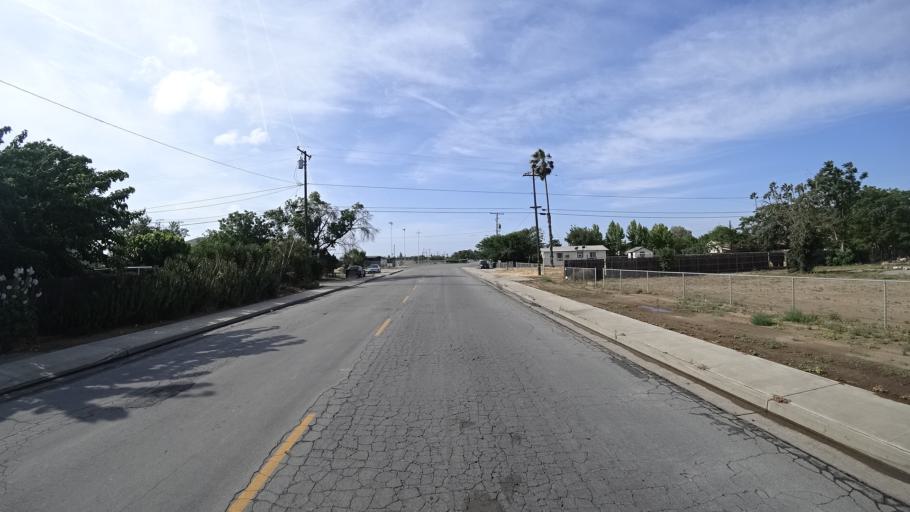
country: US
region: California
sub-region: Kings County
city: Hanford
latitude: 36.3214
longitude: -119.6429
